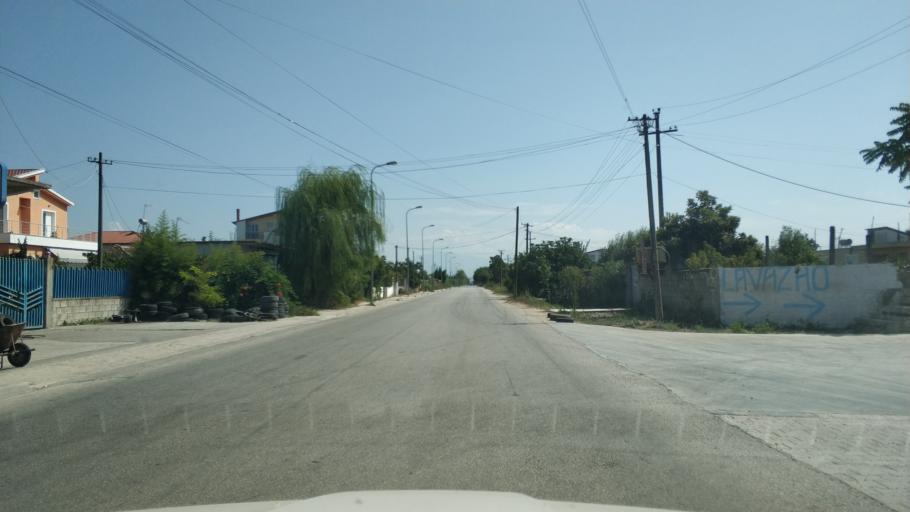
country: AL
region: Fier
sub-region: Rrethi i Lushnjes
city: Krutja e Poshtme
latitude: 40.8908
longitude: 19.6399
